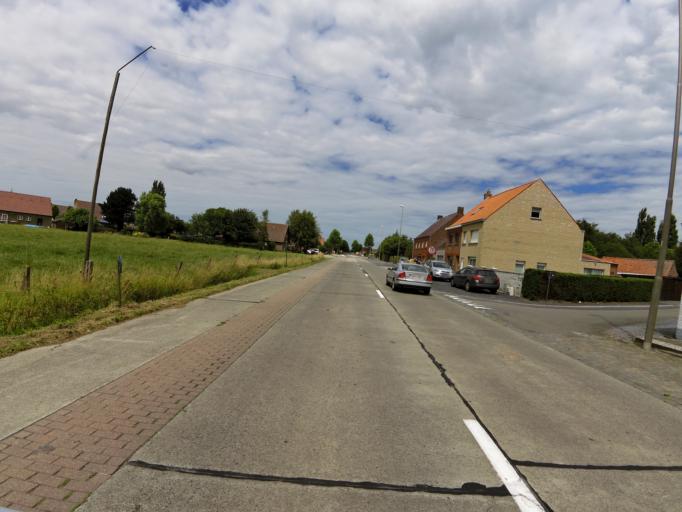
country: BE
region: Flanders
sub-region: Provincie West-Vlaanderen
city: Koekelare
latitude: 51.0814
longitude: 2.9858
